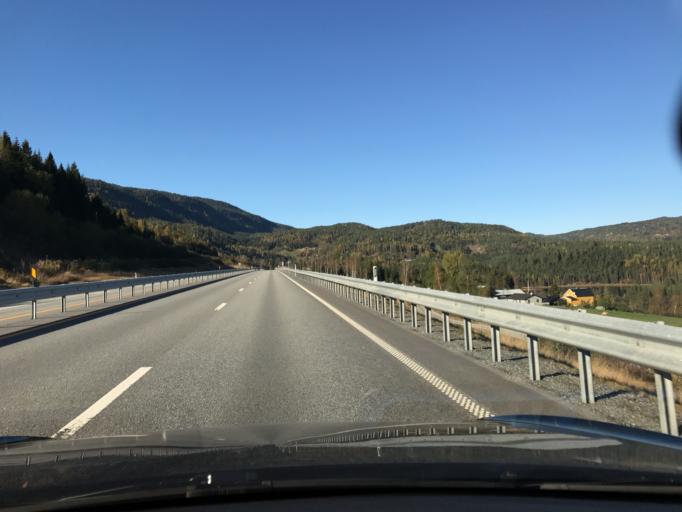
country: NO
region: Buskerud
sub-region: Krodsherad
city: Noresund
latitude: 60.2793
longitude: 9.7634
